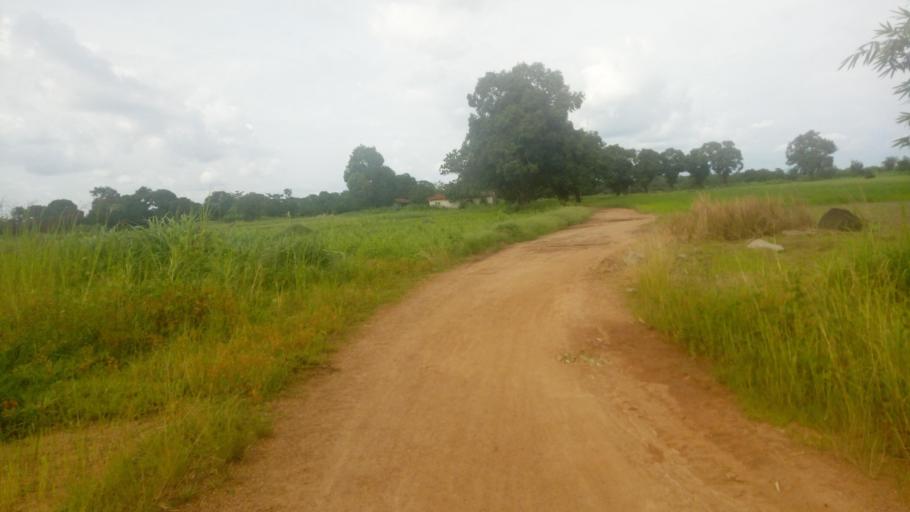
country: SL
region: Northern Province
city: Magburaka
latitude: 8.6752
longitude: -12.0137
